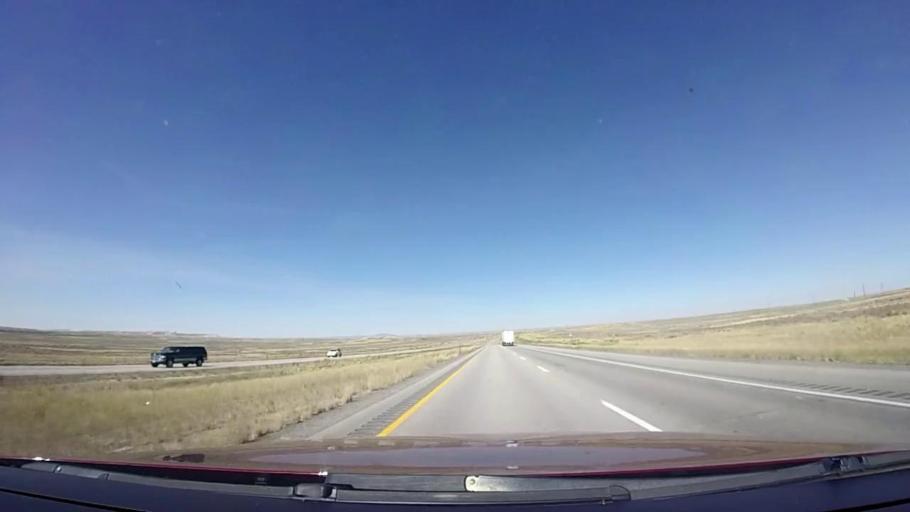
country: US
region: Wyoming
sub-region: Sweetwater County
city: Rock Springs
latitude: 41.6321
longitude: -108.3558
